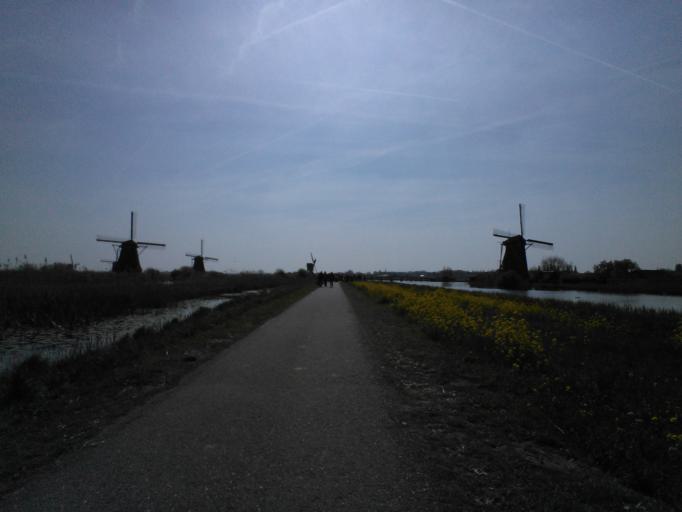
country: NL
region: South Holland
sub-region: Gemeente Alblasserdam
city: Alblasserdam
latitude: 51.8818
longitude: 4.6432
